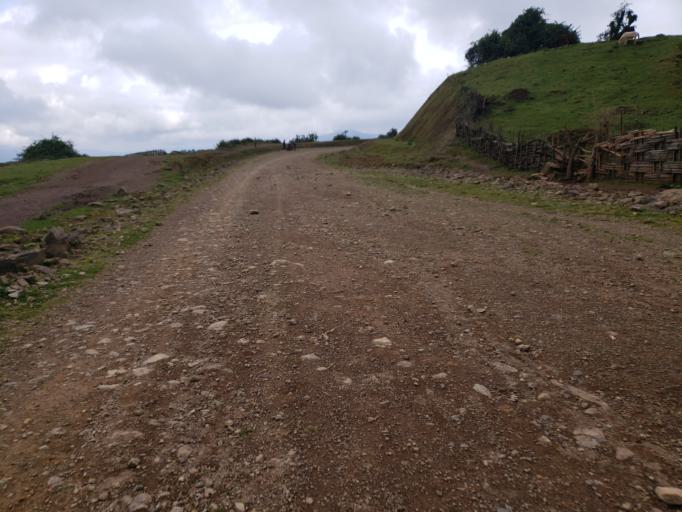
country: ET
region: Oromiya
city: Dodola
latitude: 6.6945
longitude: 39.3692
